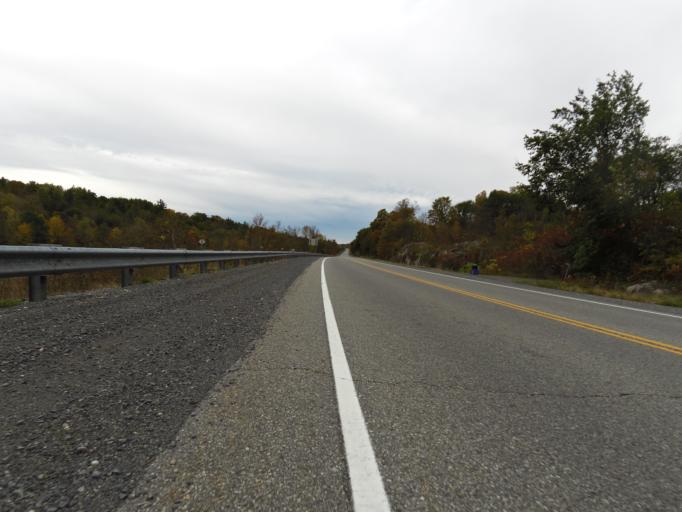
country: CA
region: Ontario
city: Gananoque
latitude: 44.3996
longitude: -76.3141
